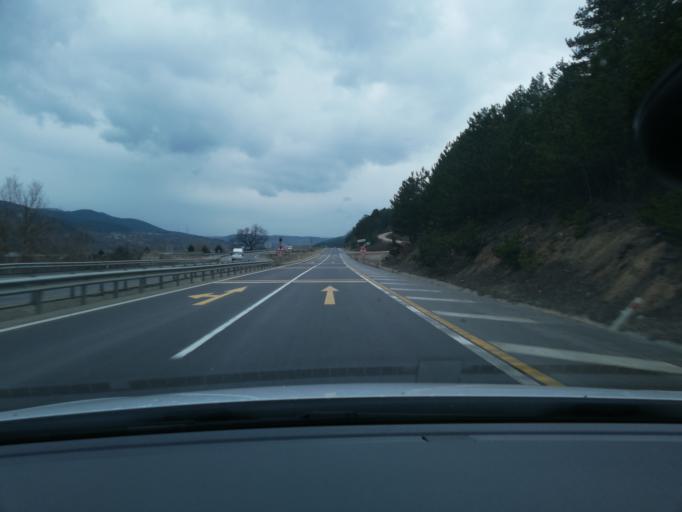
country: TR
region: Bolu
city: Yenicaga
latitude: 40.7460
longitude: 31.8715
